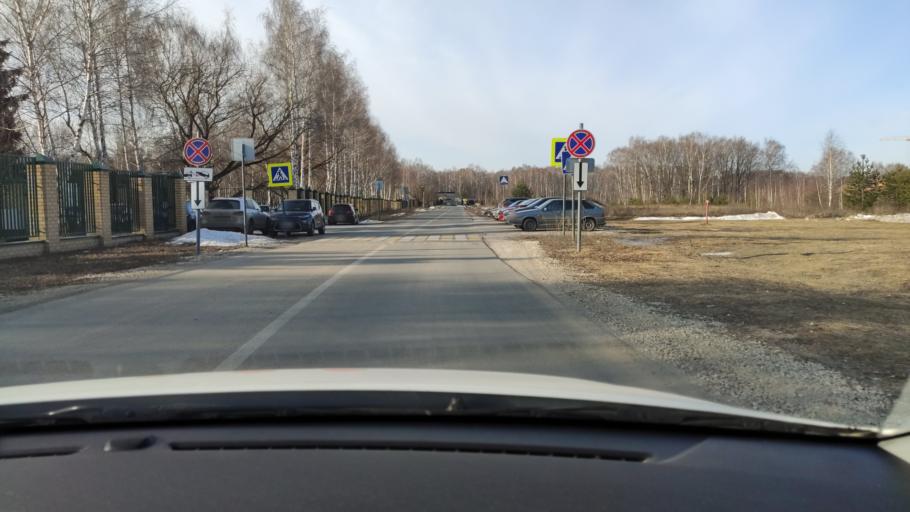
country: RU
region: Tatarstan
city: Osinovo
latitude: 55.8435
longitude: 48.9160
